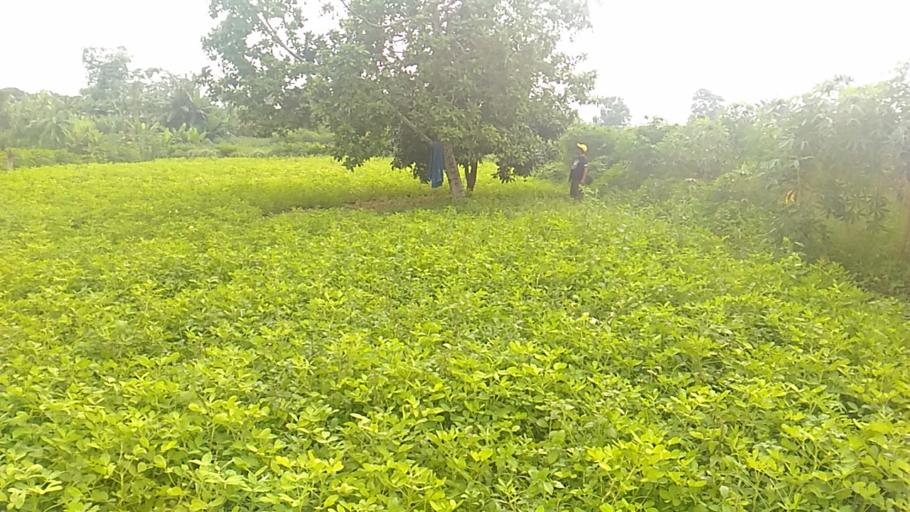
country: ID
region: North Sumatra
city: Deli Tua
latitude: 3.4902
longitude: 98.6169
